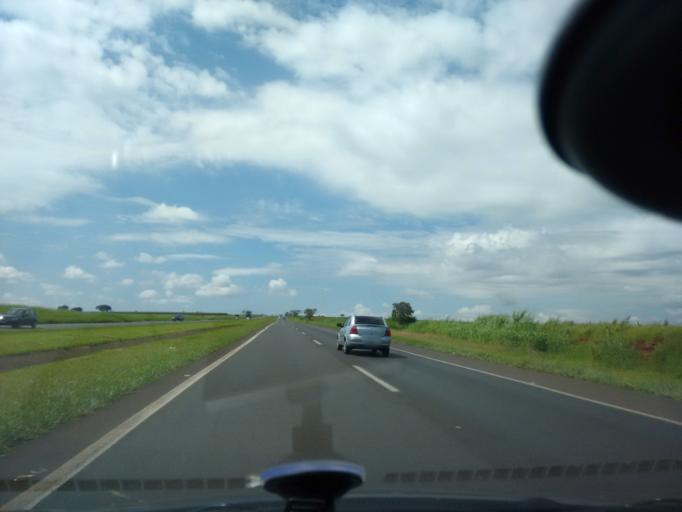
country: BR
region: Sao Paulo
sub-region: Ibate
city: Ibate
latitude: -21.8922
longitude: -48.0738
